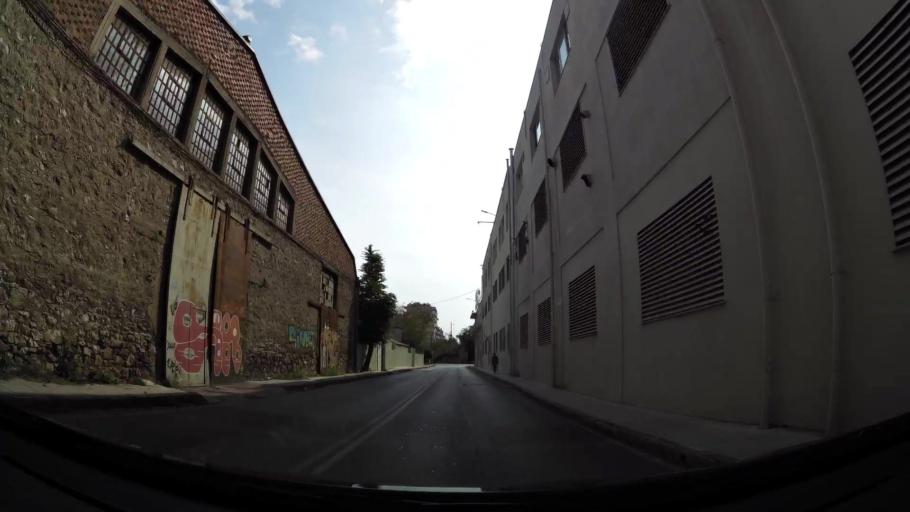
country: GR
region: Attica
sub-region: Nomarchia Athinas
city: Moskhaton
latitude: 37.9529
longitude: 23.6703
